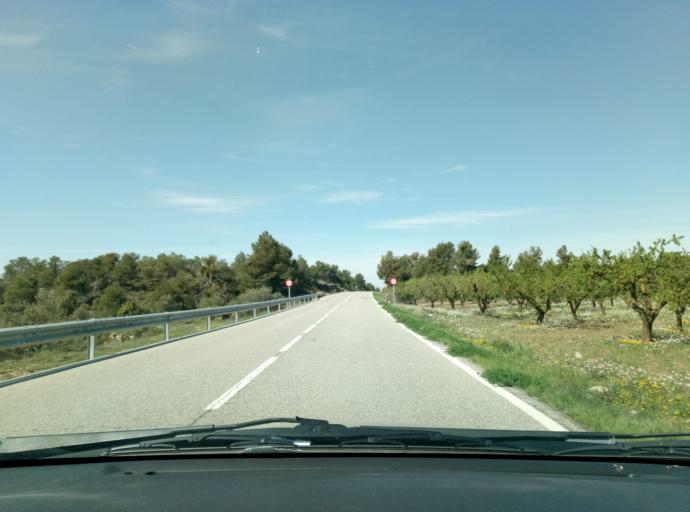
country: ES
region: Catalonia
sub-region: Provincia de Lleida
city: Fulleda
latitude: 41.5043
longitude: 1.0144
